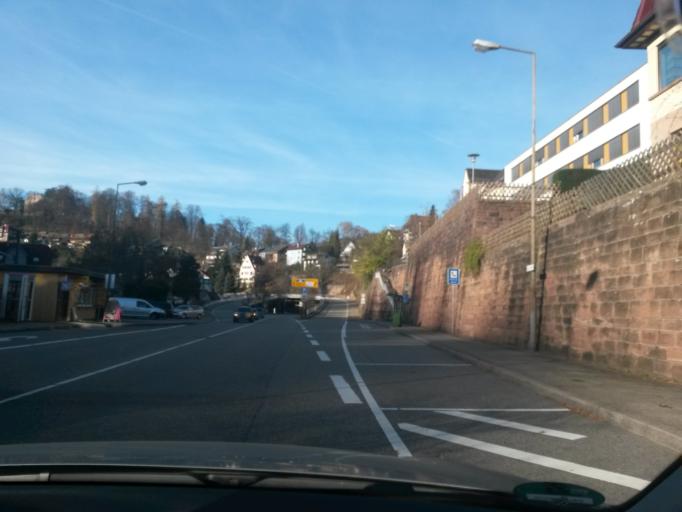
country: DE
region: Baden-Wuerttemberg
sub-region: Karlsruhe Region
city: Neuenburg
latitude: 48.8442
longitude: 8.5997
